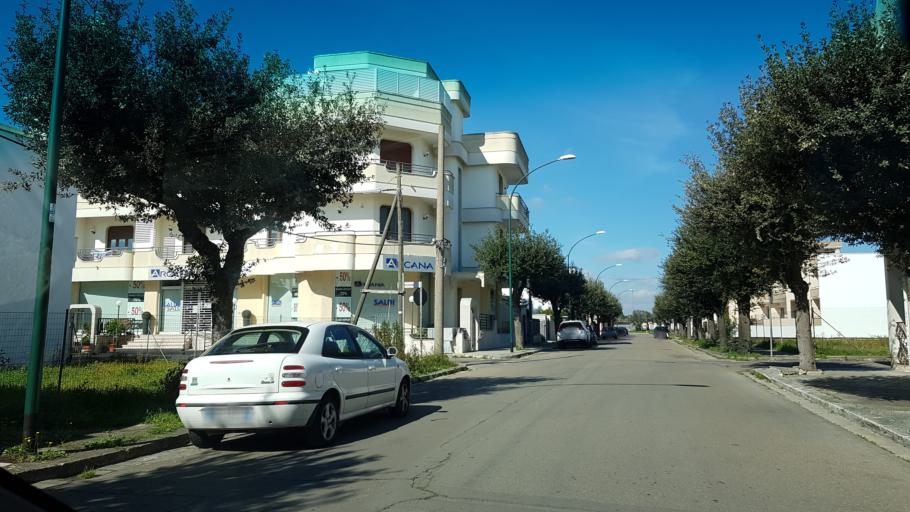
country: IT
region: Apulia
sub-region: Provincia di Lecce
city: Campi Salentina
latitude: 40.3975
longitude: 18.0104
